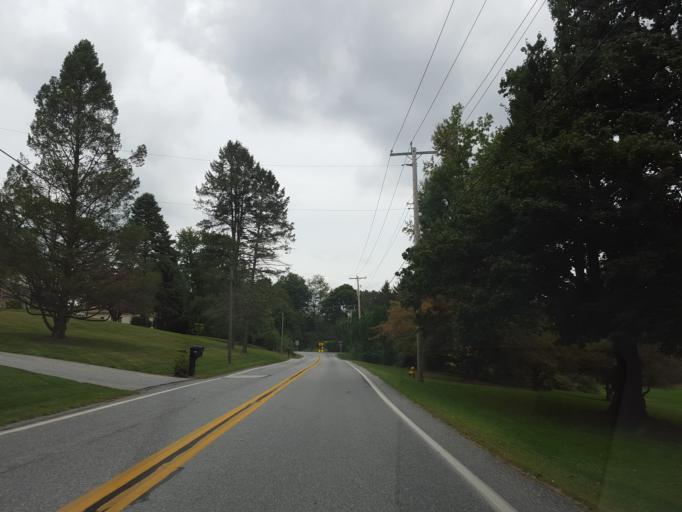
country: US
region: Pennsylvania
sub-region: York County
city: Red Lion
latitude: 39.8900
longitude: -76.6000
